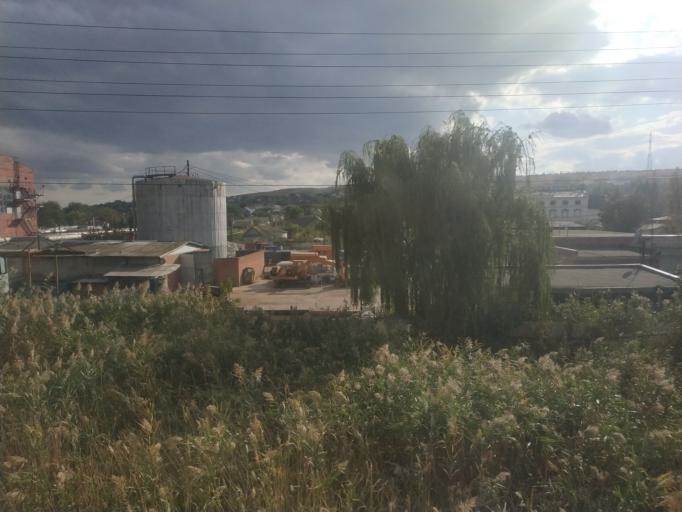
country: RU
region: Volgograd
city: Krasnoslobodsk
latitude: 48.5071
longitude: 44.5458
